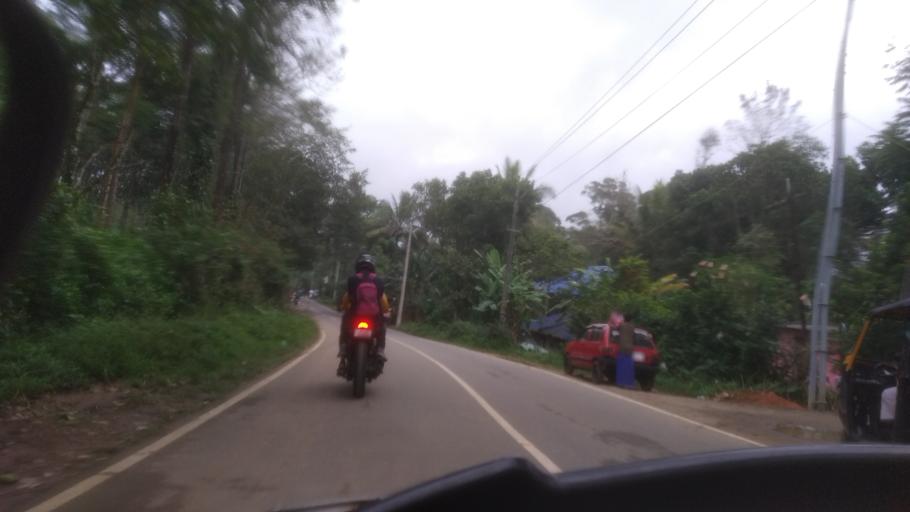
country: IN
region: Tamil Nadu
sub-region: Theni
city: Kombai
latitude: 9.8993
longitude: 77.1811
